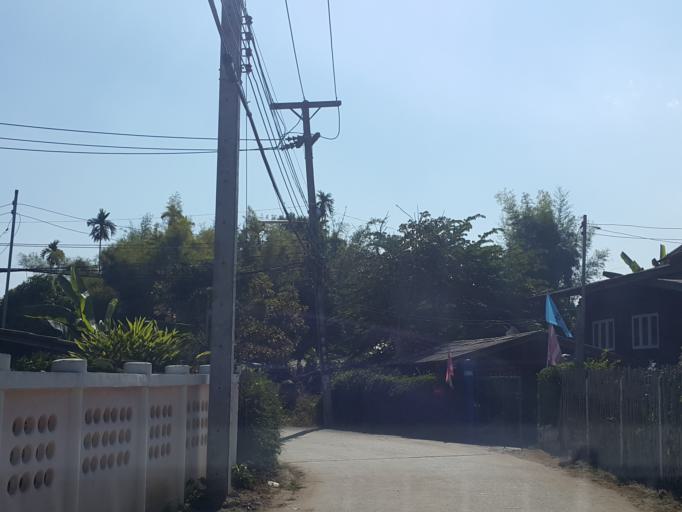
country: TH
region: Chiang Mai
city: San Sai
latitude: 18.8828
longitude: 98.9952
